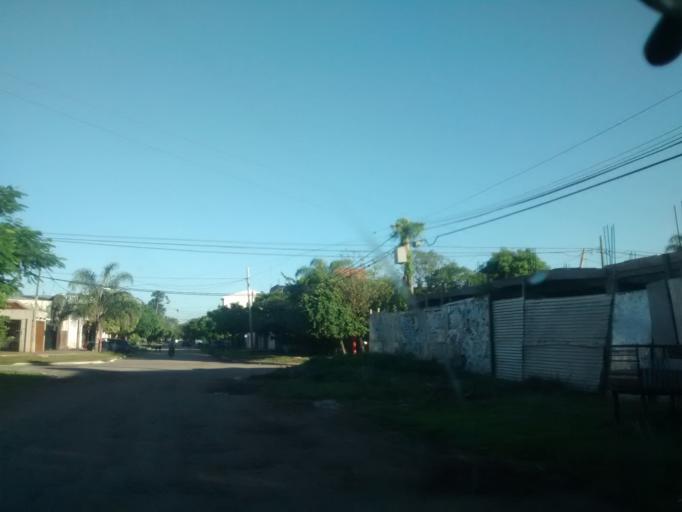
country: AR
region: Chaco
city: Resistencia
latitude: -27.4673
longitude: -58.9935
